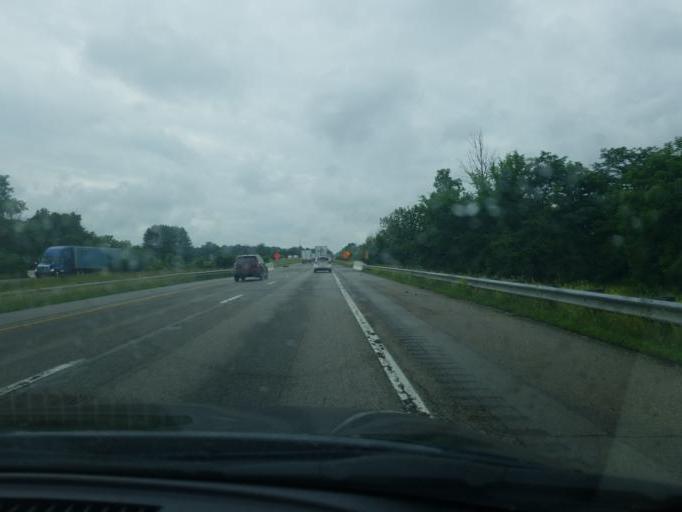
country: US
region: Ohio
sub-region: Warren County
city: Waynesville
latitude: 39.4416
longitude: -84.0479
